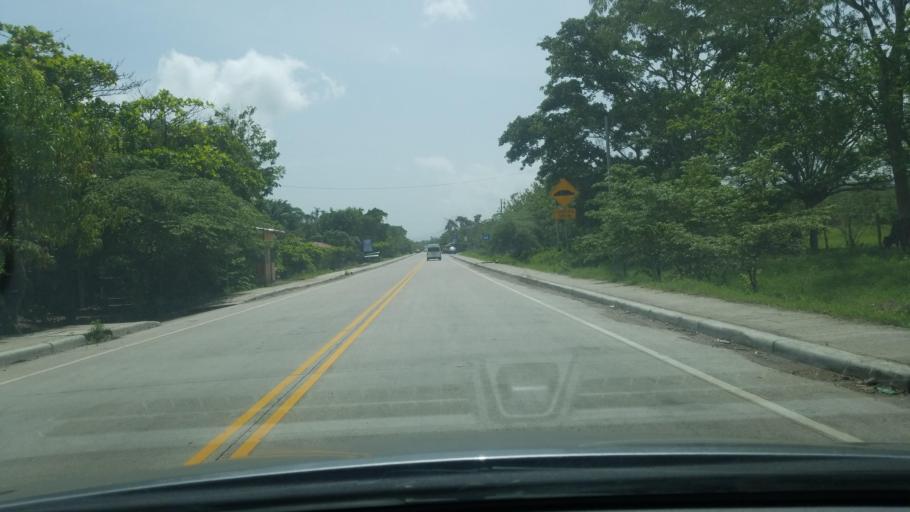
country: HN
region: Copan
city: Florida
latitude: 15.0442
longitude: -88.8114
